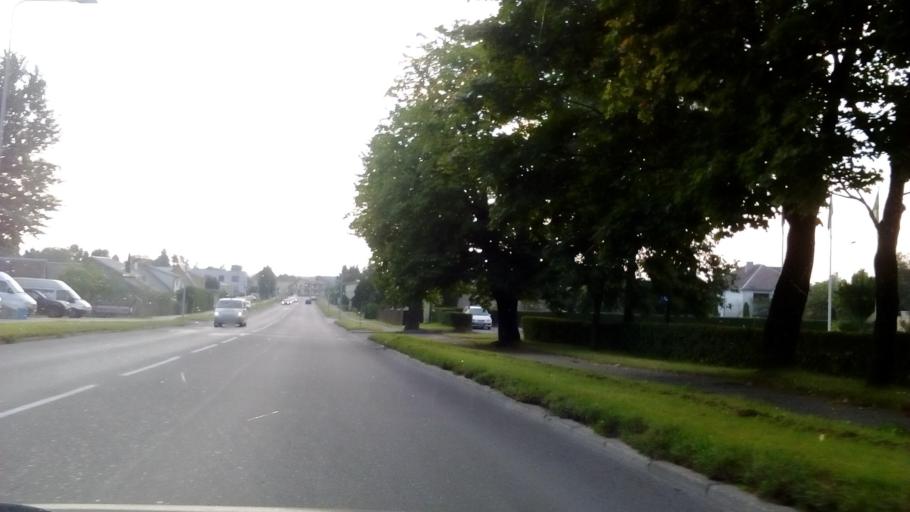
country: LT
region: Alytaus apskritis
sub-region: Alytus
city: Alytus
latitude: 54.3869
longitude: 24.0363
